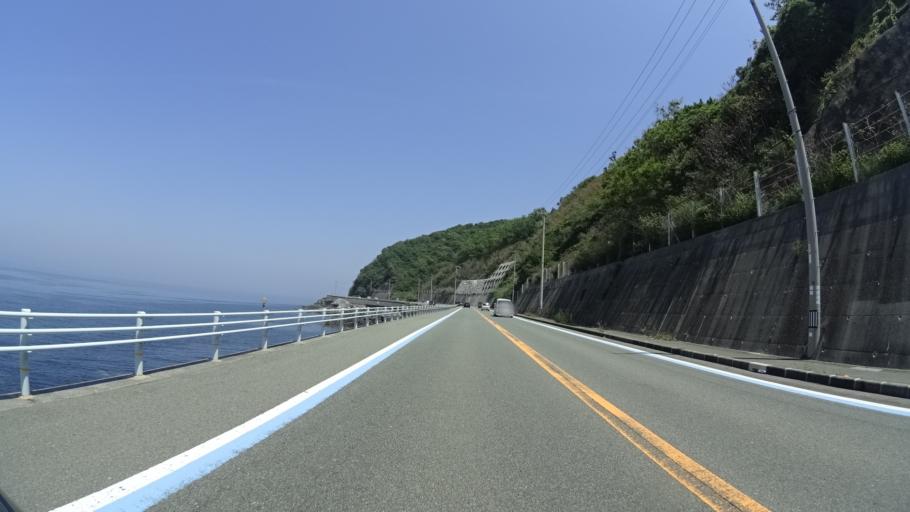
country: JP
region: Ehime
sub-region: Nishiuwa-gun
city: Ikata-cho
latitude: 33.5646
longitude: 132.4333
